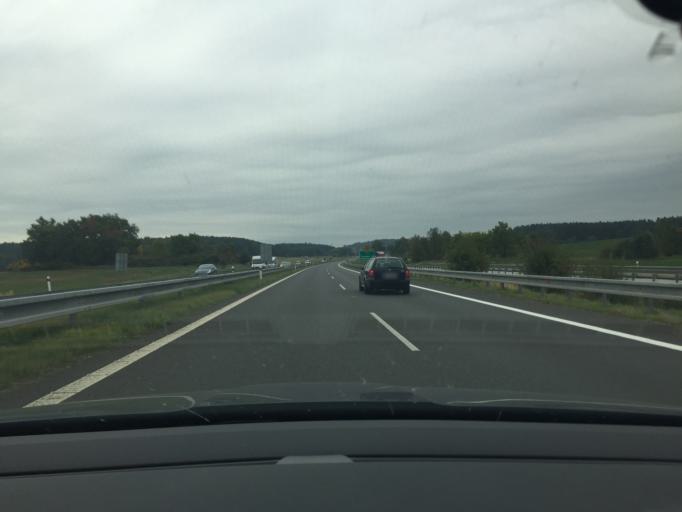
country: CZ
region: Jihocesky
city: Mirotice
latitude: 49.4111
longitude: 14.0385
